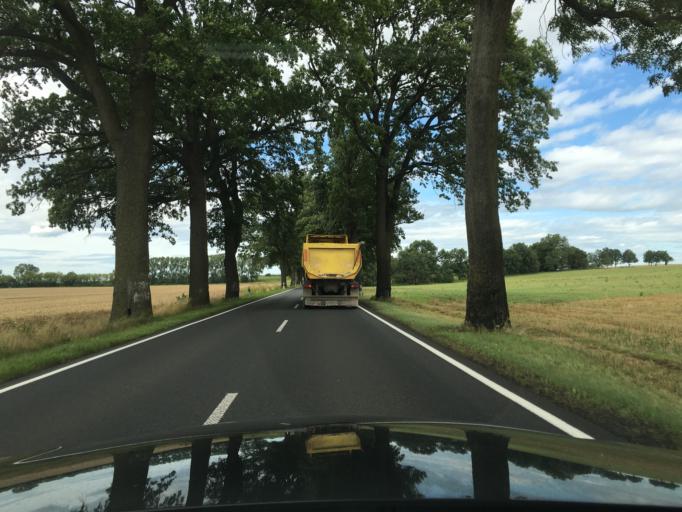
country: DE
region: Brandenburg
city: Gransee
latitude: 52.9347
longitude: 13.1544
